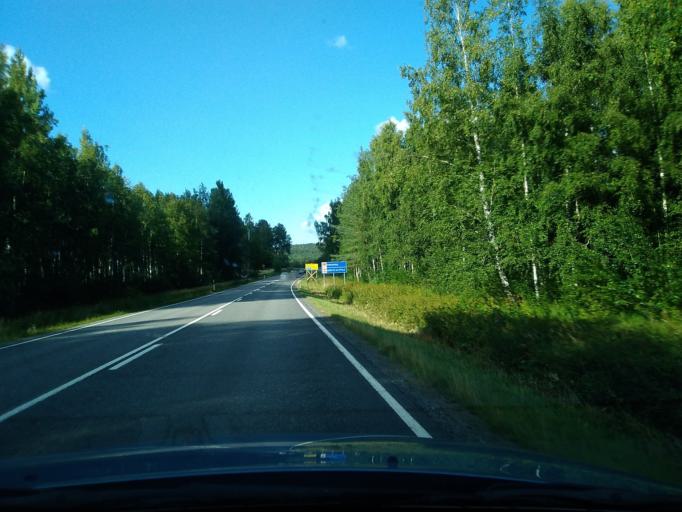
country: FI
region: Pirkanmaa
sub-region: Ylae-Pirkanmaa
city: Maenttae
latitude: 61.9931
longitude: 24.6361
